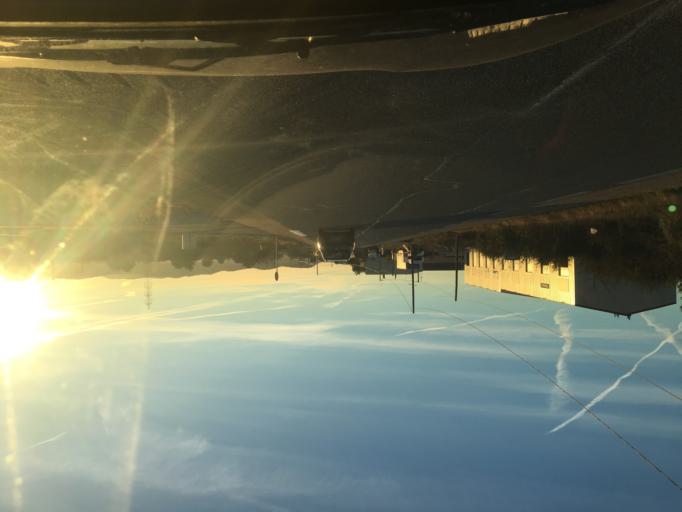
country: FR
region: Provence-Alpes-Cote d'Azur
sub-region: Departement du Var
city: Les Arcs
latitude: 43.4506
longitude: 6.4608
